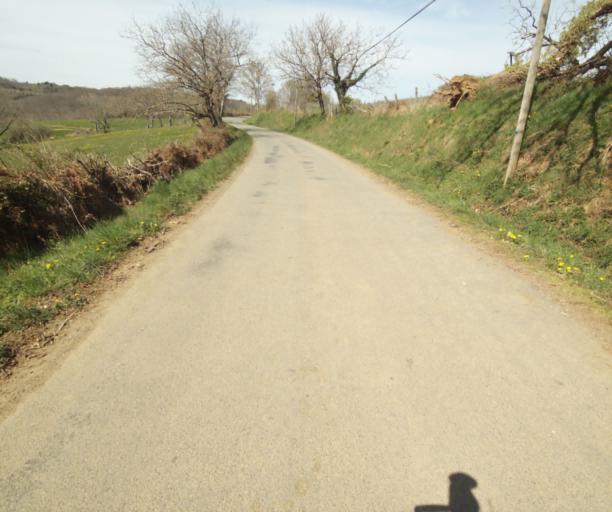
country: FR
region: Limousin
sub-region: Departement de la Correze
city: Seilhac
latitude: 45.3879
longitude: 1.7813
